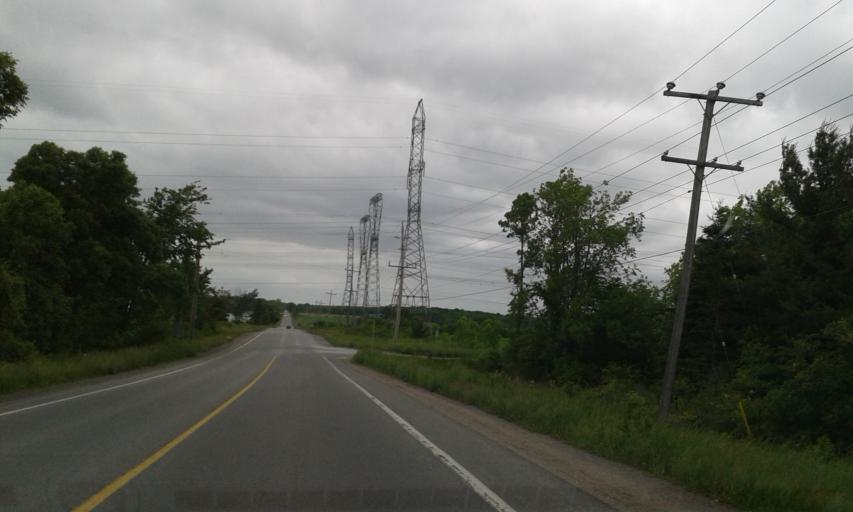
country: CA
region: Ontario
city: Skatepark
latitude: 44.1996
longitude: -76.7864
